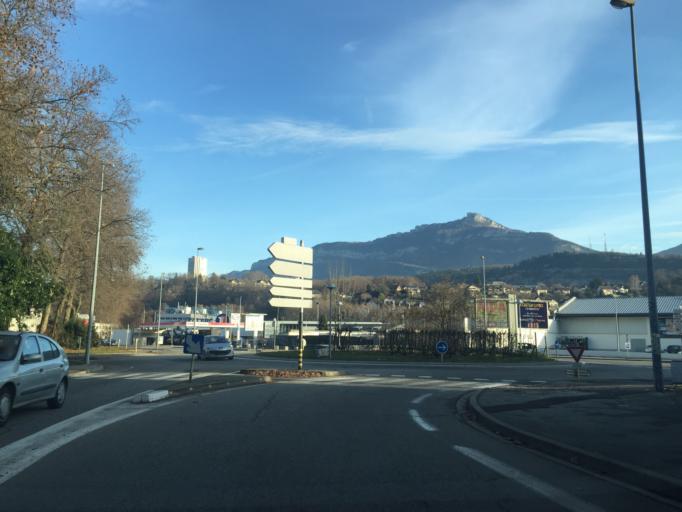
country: FR
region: Rhone-Alpes
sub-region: Departement de la Savoie
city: Cognin
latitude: 45.5782
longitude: 5.9087
